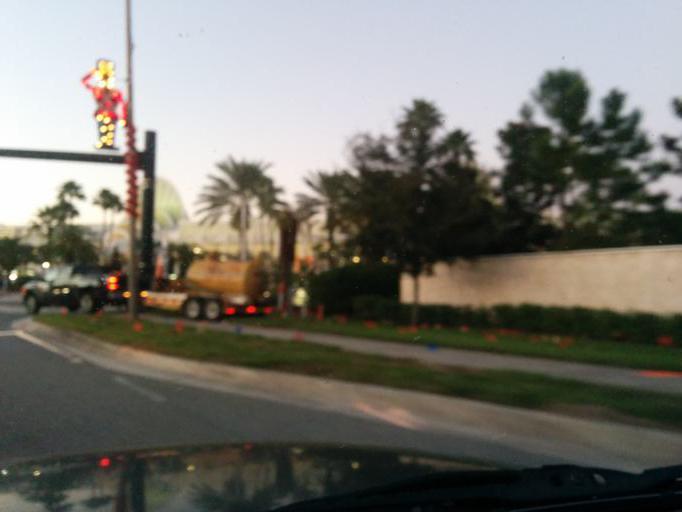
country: US
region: Florida
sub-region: Orange County
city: Williamsburg
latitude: 28.4250
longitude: -81.4612
